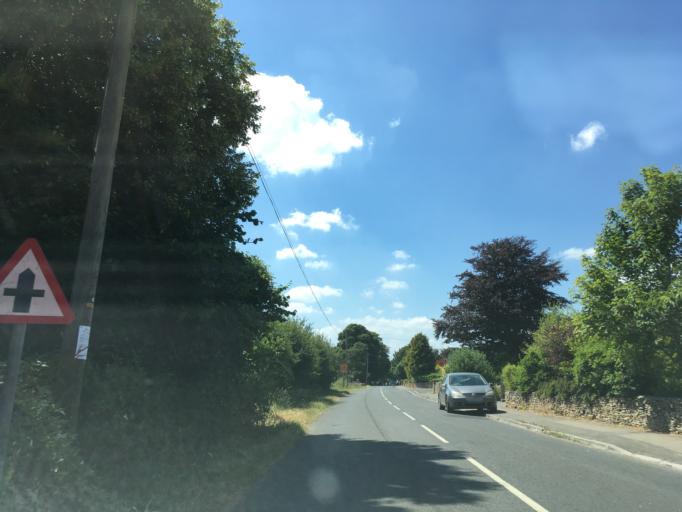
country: GB
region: England
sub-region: Gloucestershire
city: Chalford
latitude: 51.7364
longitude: -2.1552
